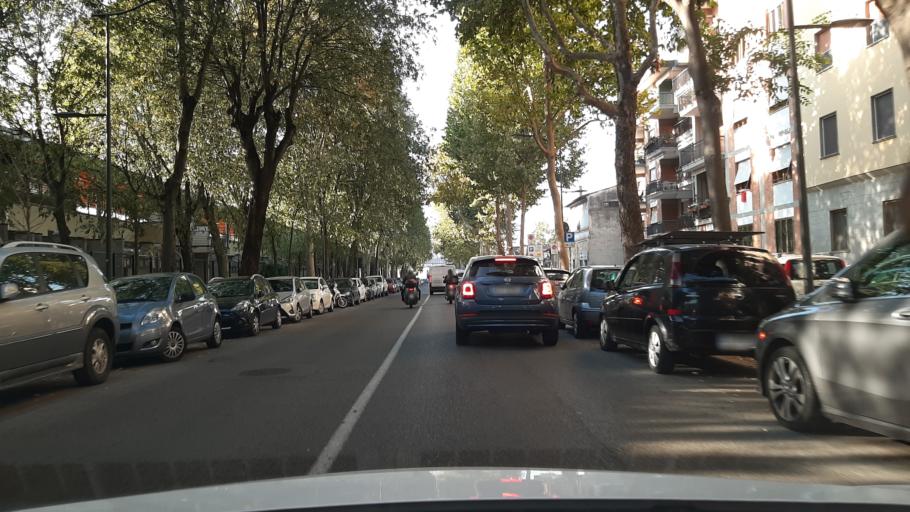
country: IT
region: Tuscany
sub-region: Province of Florence
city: Fiesole
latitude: 43.7796
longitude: 11.2802
